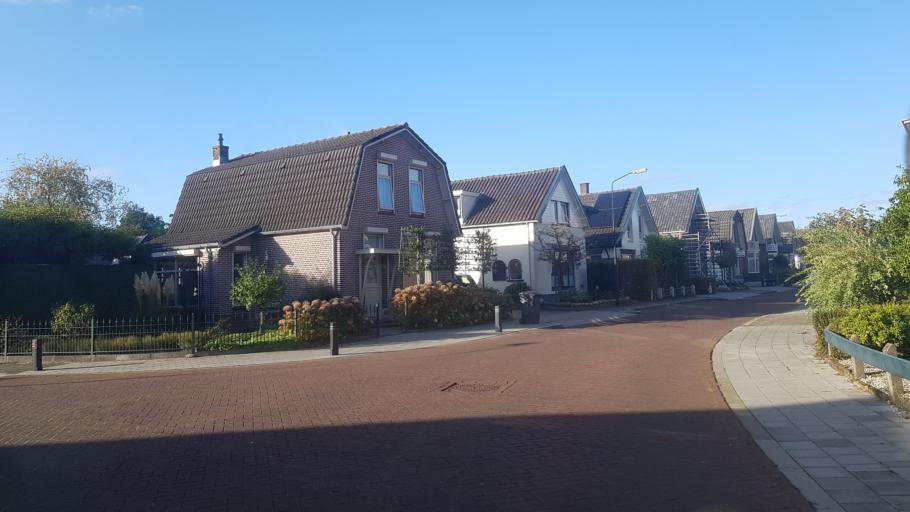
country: NL
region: Gelderland
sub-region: Gemeente Apeldoorn
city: Apeldoorn
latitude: 52.2073
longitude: 5.9454
